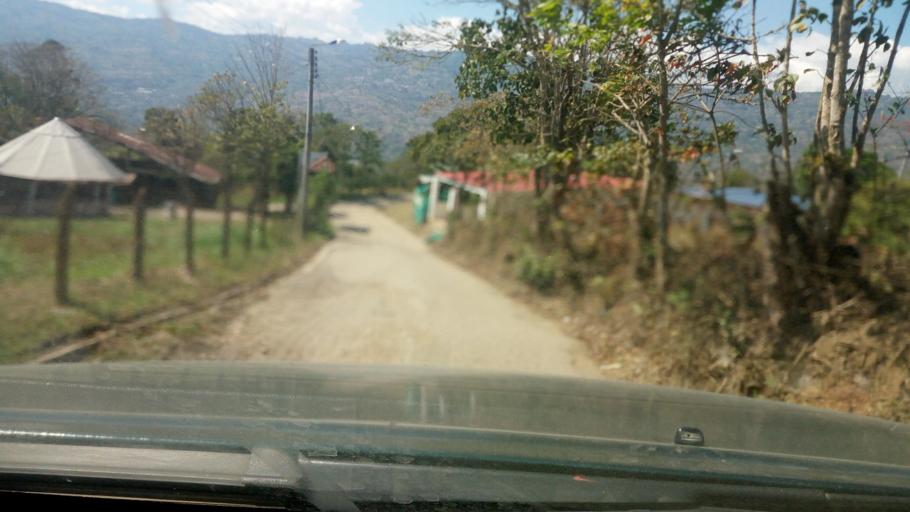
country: CO
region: Boyaca
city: Somondoco
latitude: 4.9856
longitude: -73.4354
